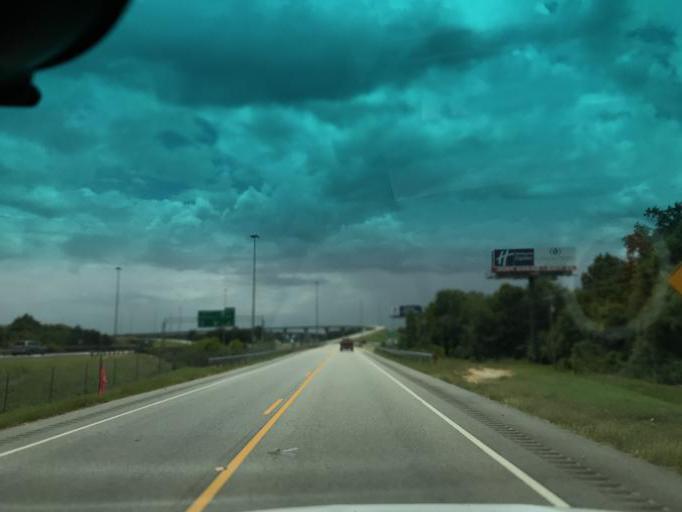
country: US
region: Alabama
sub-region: Montgomery County
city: Pike Road
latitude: 32.3686
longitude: -86.0686
